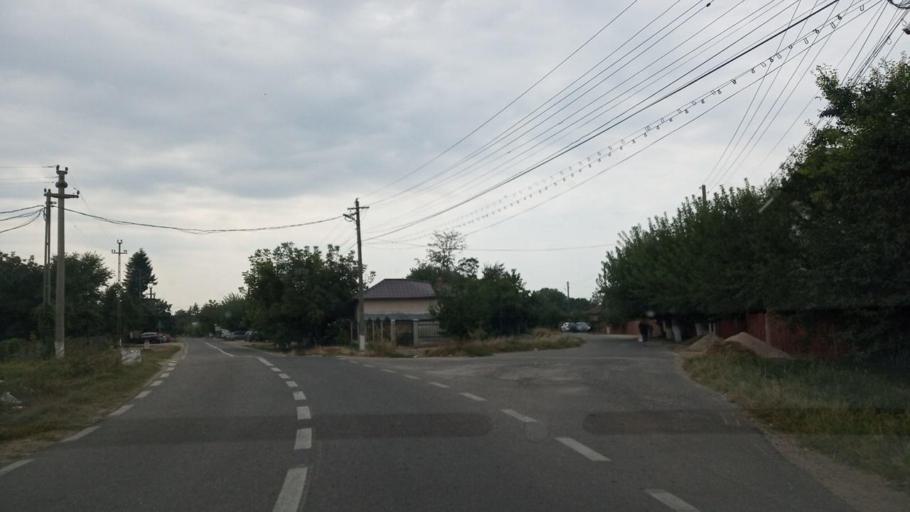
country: RO
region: Giurgiu
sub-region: Comuna Izvoarele
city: Isvoarele
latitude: 44.1699
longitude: 26.3115
